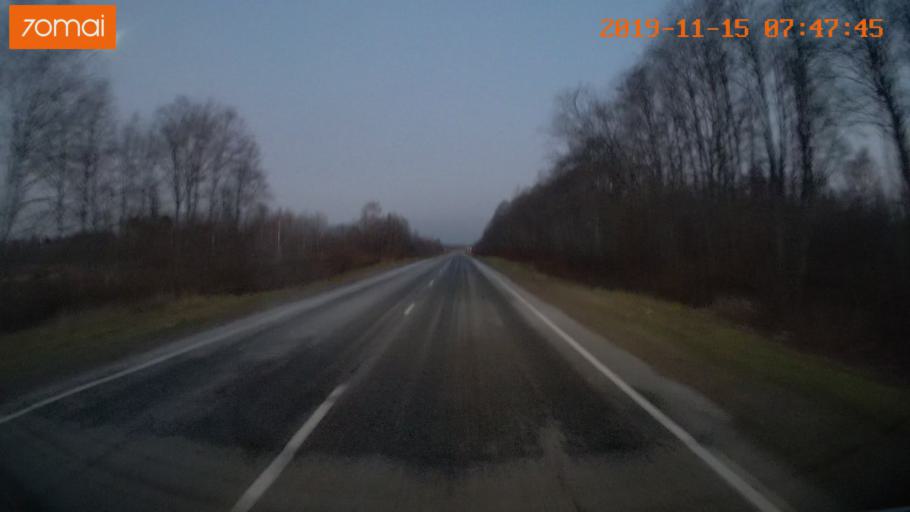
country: RU
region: Vologda
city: Sheksna
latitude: 58.8441
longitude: 38.2560
